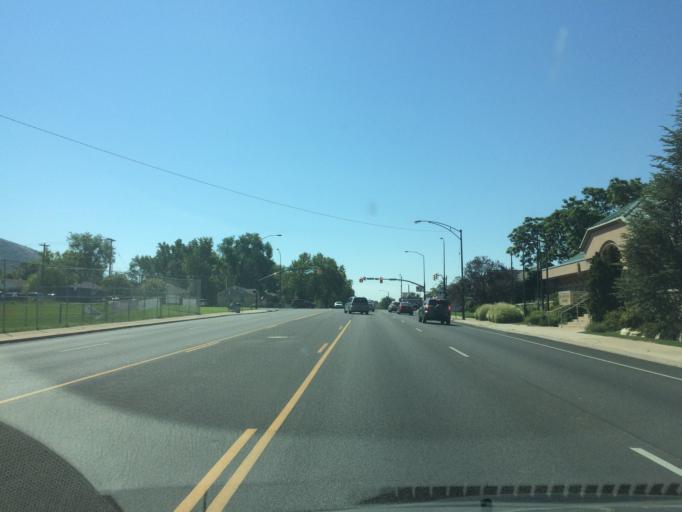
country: US
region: Utah
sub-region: Weber County
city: Ogden
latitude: 41.2111
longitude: -111.9485
